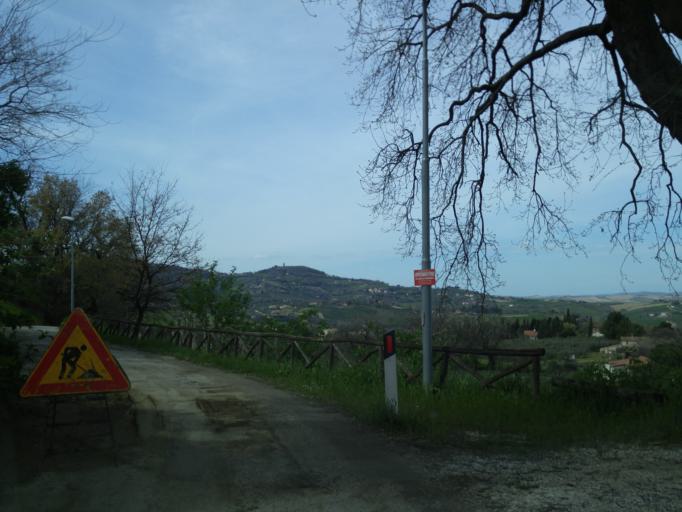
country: IT
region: The Marches
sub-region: Provincia di Pesaro e Urbino
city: Cartoceto
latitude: 43.7661
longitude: 12.8968
